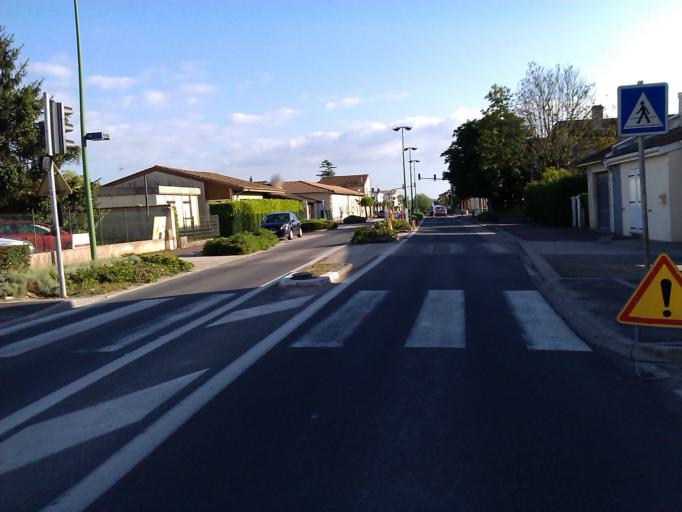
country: FR
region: Aquitaine
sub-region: Departement de la Gironde
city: Cubzac-les-Ponts
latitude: 44.9727
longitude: -0.4528
